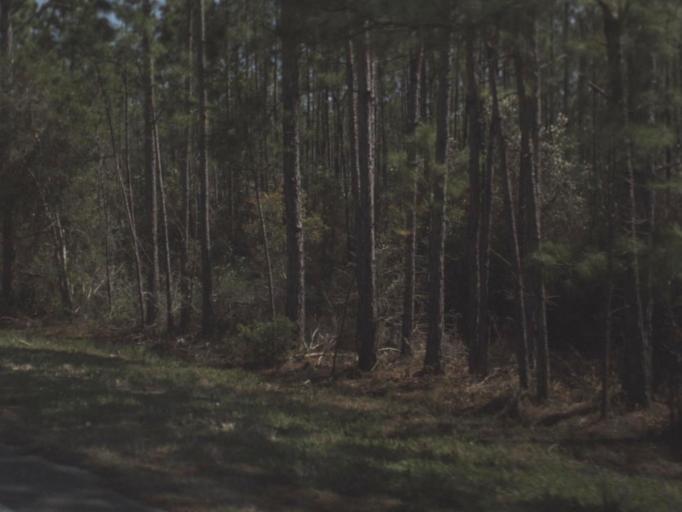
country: US
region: Florida
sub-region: Gulf County
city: Port Saint Joe
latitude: 29.7378
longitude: -85.1770
